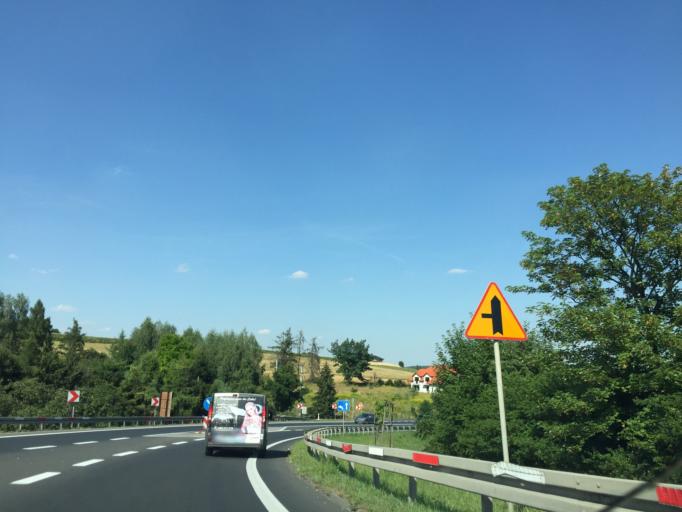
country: PL
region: Lesser Poland Voivodeship
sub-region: Powiat krakowski
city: Michalowice
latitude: 50.1462
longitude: 19.9755
